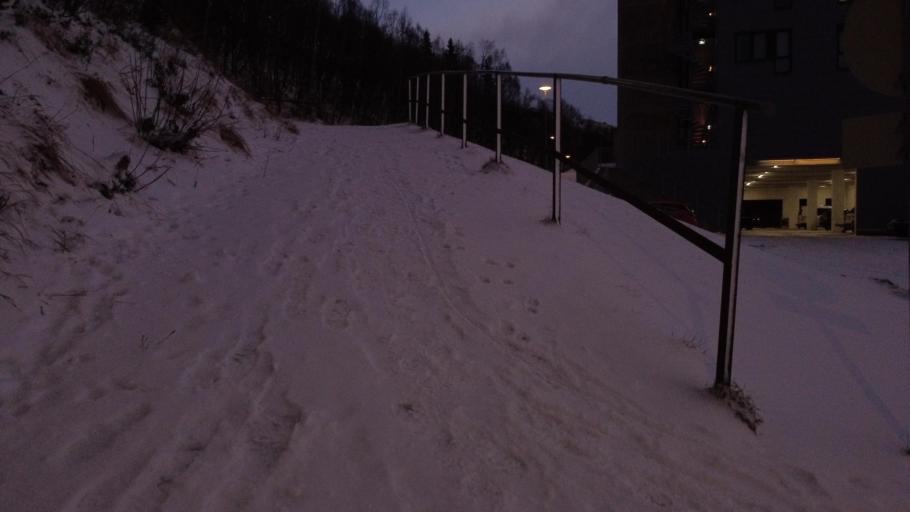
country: NO
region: Nordland
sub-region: Rana
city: Mo i Rana
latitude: 66.3195
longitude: 14.1557
